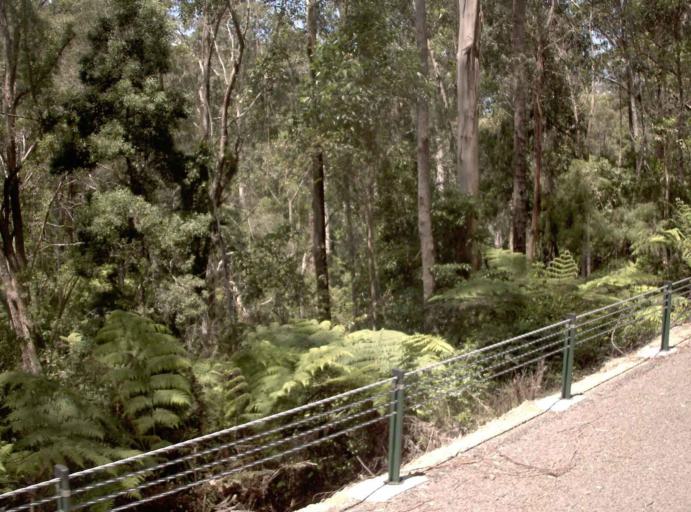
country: AU
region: New South Wales
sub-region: Bombala
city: Bombala
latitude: -37.5832
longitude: 148.9283
